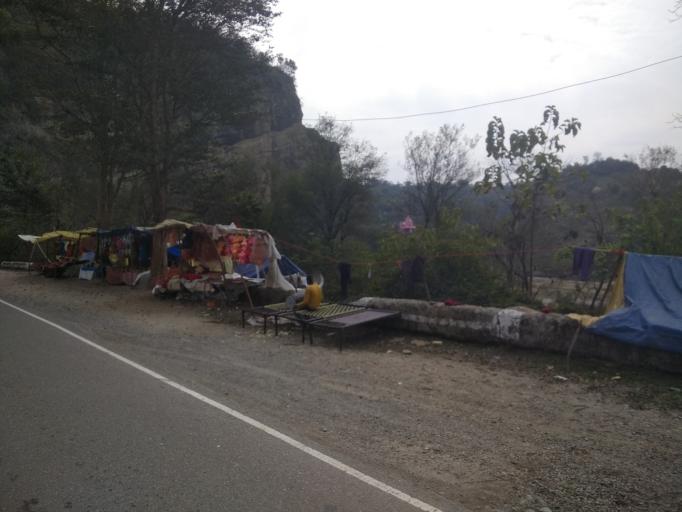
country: IN
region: Himachal Pradesh
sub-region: Kangra
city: Kotla
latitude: 32.2302
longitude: 76.0571
